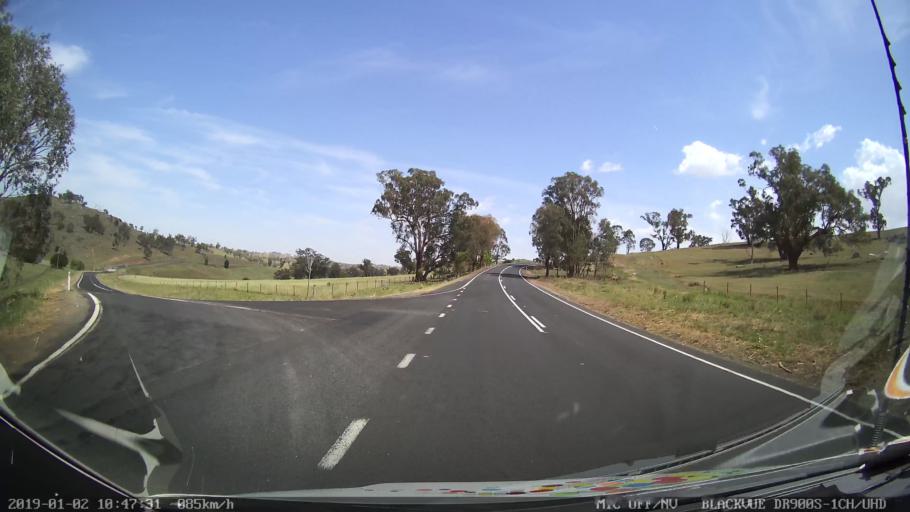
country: AU
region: New South Wales
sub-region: Cootamundra
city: Cootamundra
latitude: -34.7443
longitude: 148.2728
